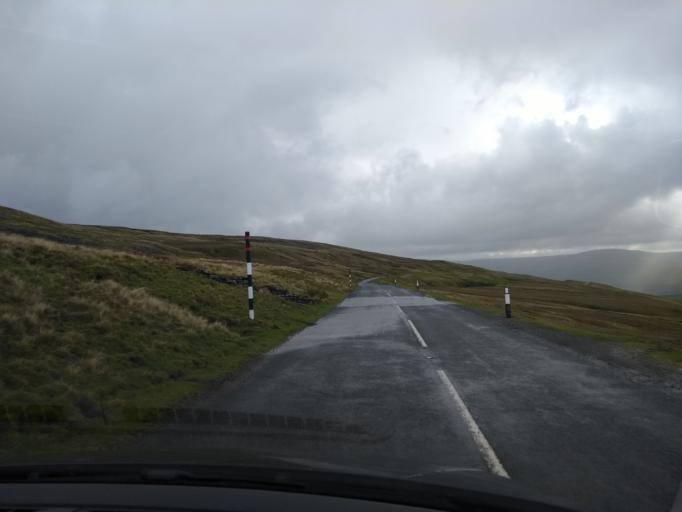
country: GB
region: England
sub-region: Cumbria
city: Kirkby Stephen
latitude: 54.3487
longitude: -2.2044
